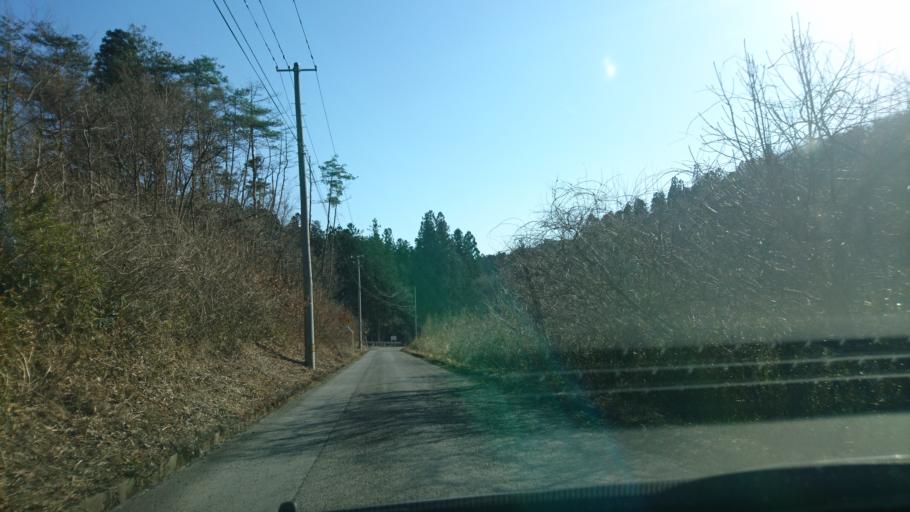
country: JP
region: Iwate
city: Ichinoseki
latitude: 38.8038
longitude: 141.2650
